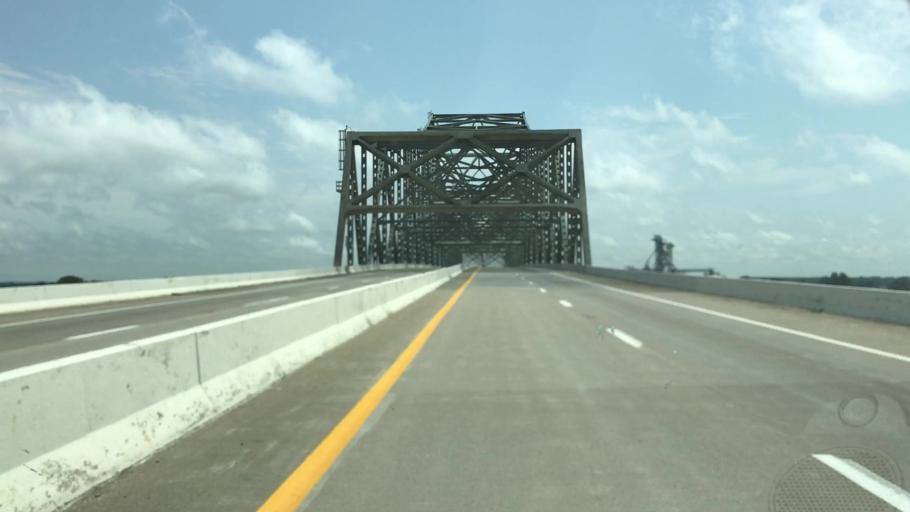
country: US
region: Missouri
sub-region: Pemiscot County
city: Caruthersville
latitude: 36.1161
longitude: -89.6138
